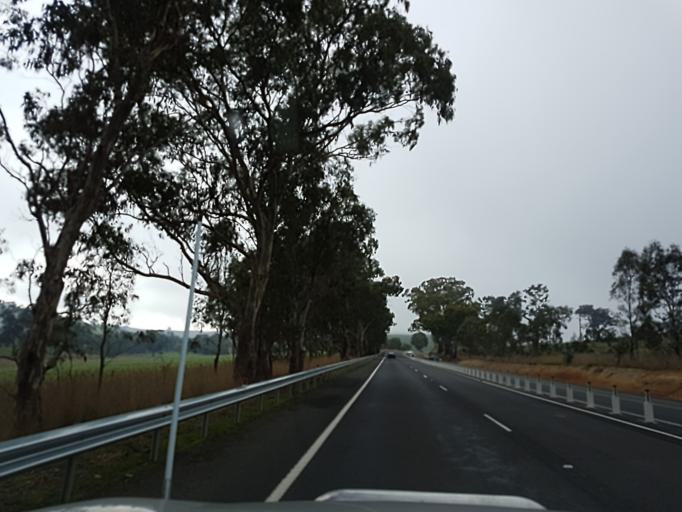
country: AU
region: Victoria
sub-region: Murrindindi
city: Alexandra
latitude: -37.1988
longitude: 145.4722
